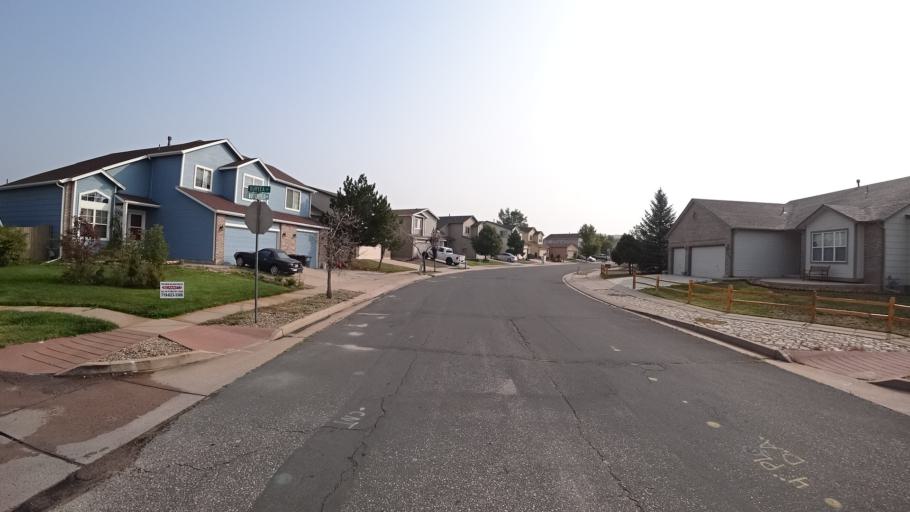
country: US
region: Colorado
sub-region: El Paso County
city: Black Forest
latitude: 38.9368
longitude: -104.7290
